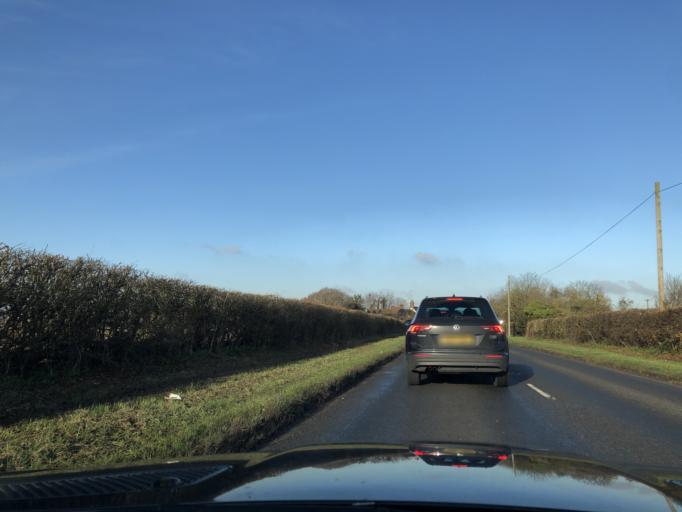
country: GB
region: England
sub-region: Buckinghamshire
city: High Wycombe
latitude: 51.6068
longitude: -0.7708
